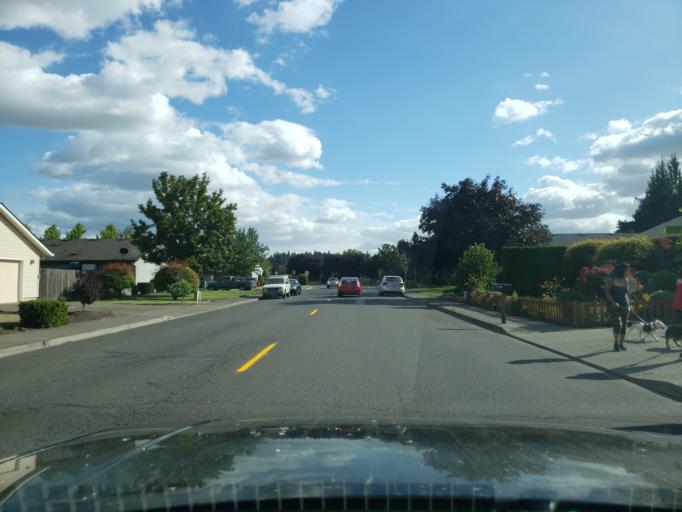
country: US
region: Oregon
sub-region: Yamhill County
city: McMinnville
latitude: 45.2024
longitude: -123.2197
